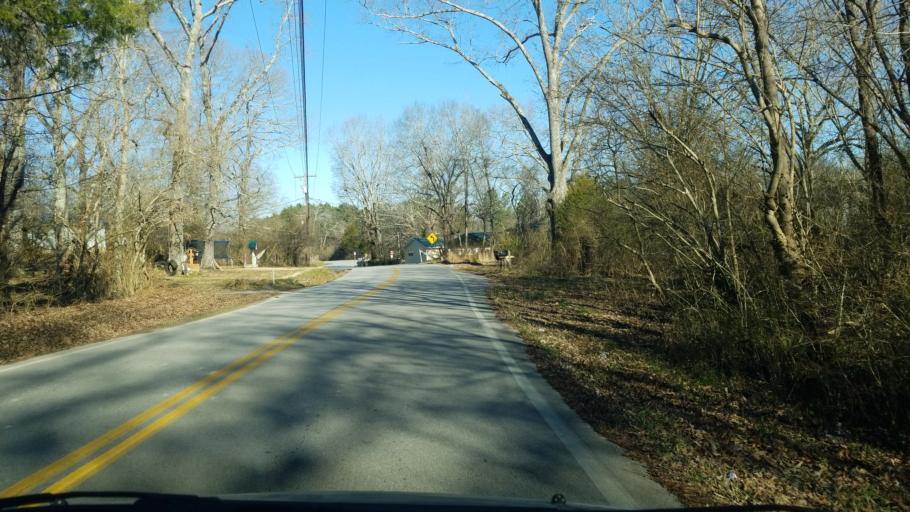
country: US
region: Tennessee
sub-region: Hamilton County
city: Collegedale
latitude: 35.0623
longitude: -85.0967
